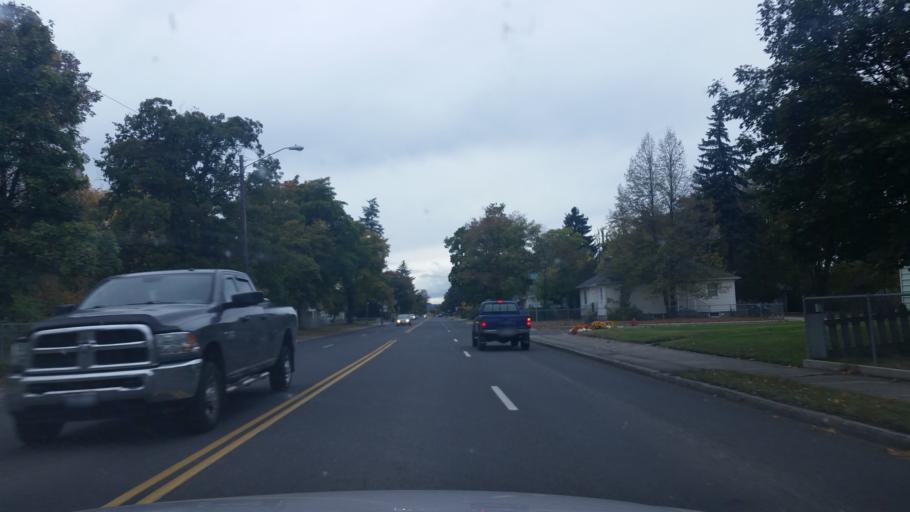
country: US
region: Washington
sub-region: Spokane County
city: Spokane
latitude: 47.6719
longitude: -117.3719
